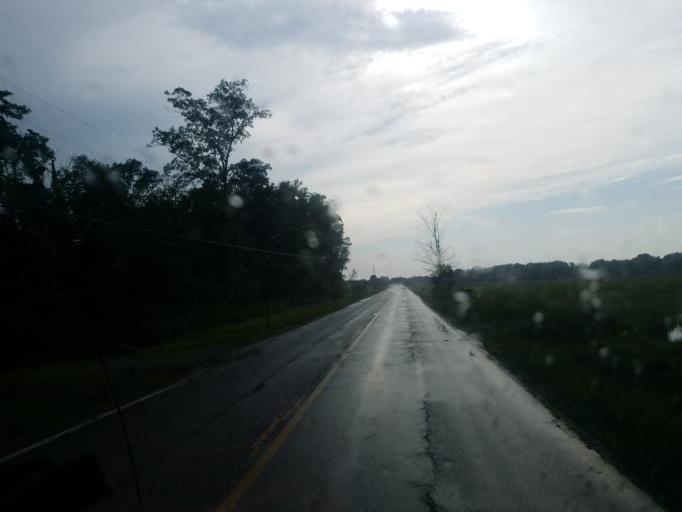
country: US
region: Ohio
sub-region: Wayne County
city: Creston
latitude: 40.9446
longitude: -81.9736
